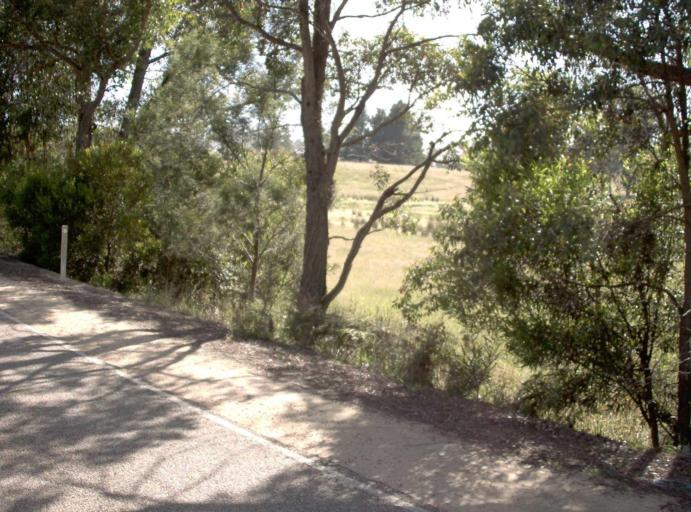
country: AU
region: Victoria
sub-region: East Gippsland
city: Lakes Entrance
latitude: -37.5313
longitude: 148.1534
